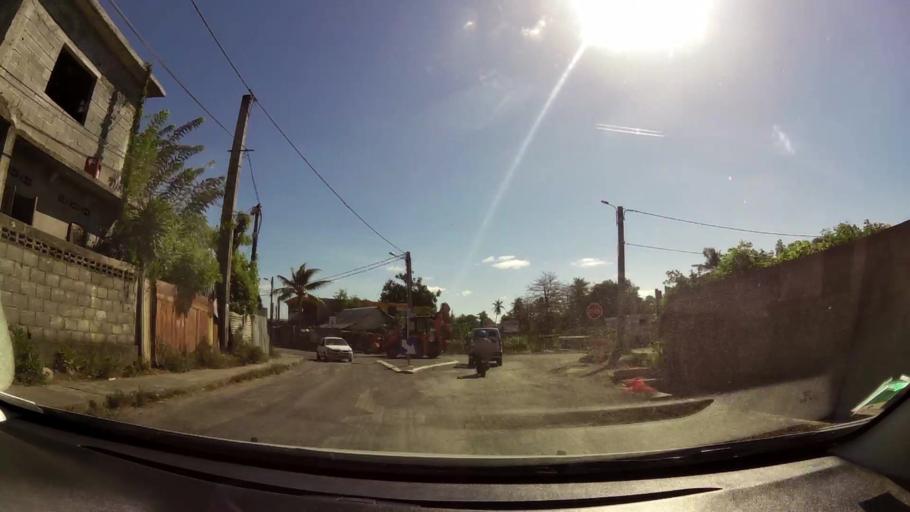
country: YT
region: Pamandzi
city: Pamandzi
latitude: -12.7862
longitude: 45.2736
